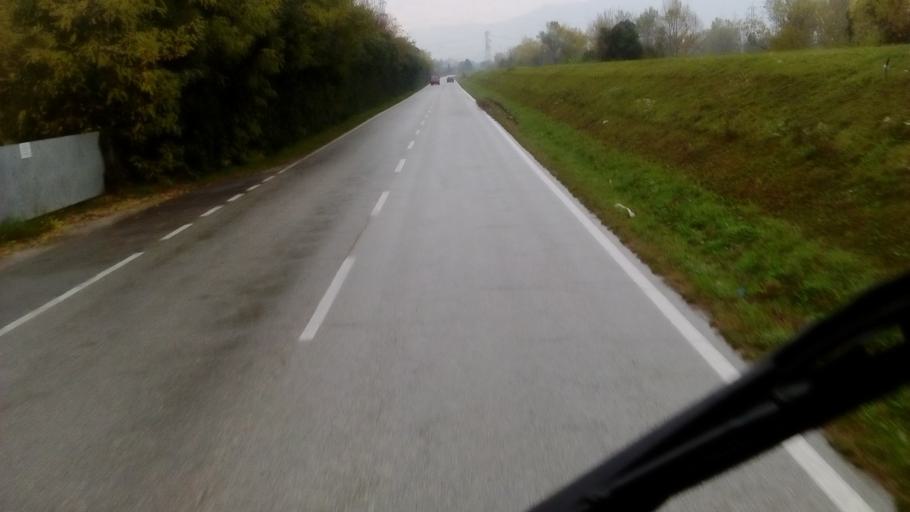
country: IT
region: Veneto
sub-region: Provincia di Vicenza
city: Sandrigo
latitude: 45.6518
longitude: 11.5770
